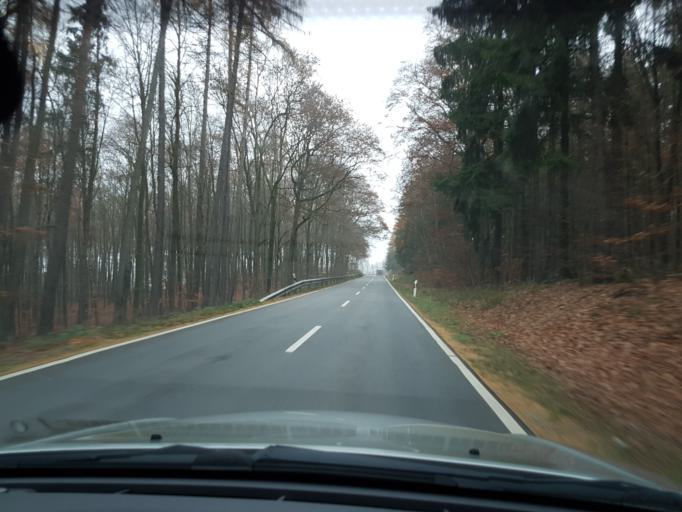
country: DE
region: Hesse
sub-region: Regierungsbezirk Darmstadt
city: Bad Schwalbach
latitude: 50.1189
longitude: 8.0389
